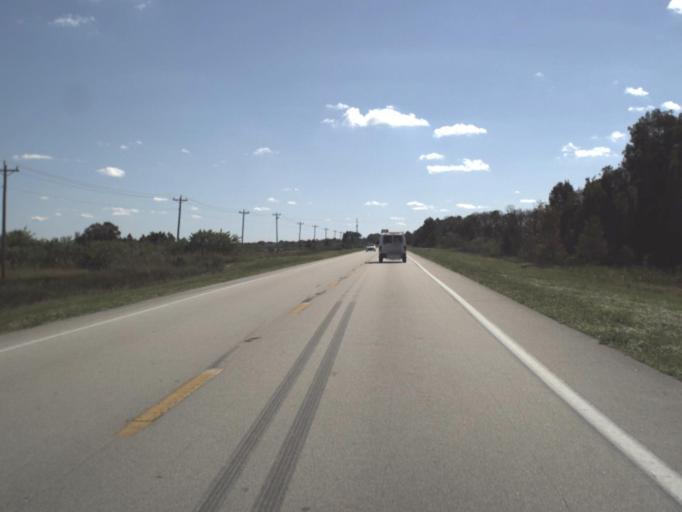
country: US
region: Florida
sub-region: Lee County
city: Lehigh Acres
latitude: 26.5179
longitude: -81.5615
